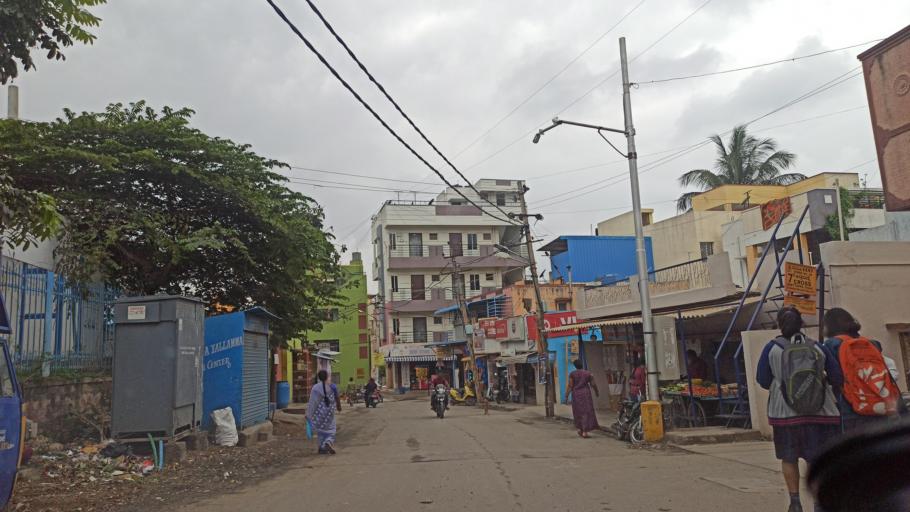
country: IN
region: Karnataka
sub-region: Bangalore Urban
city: Bangalore
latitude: 12.9958
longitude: 77.6755
